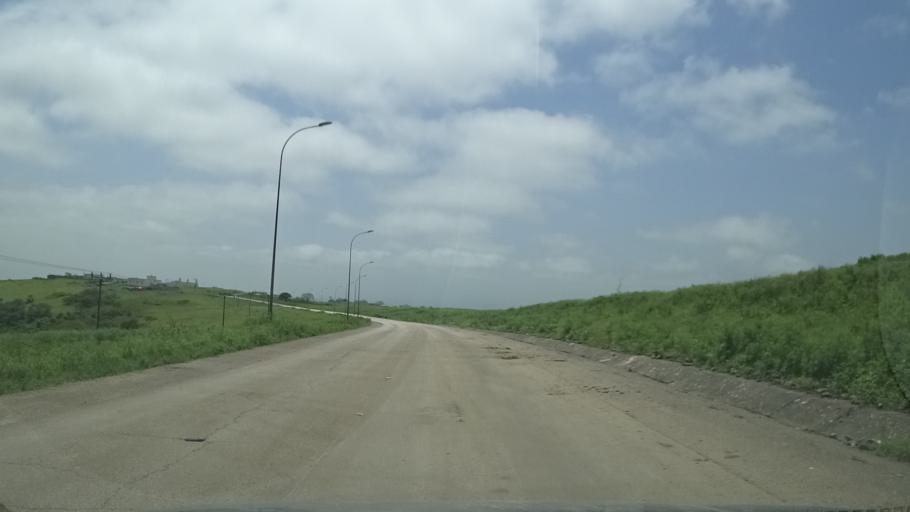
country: OM
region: Zufar
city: Salalah
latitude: 17.2198
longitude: 54.2541
